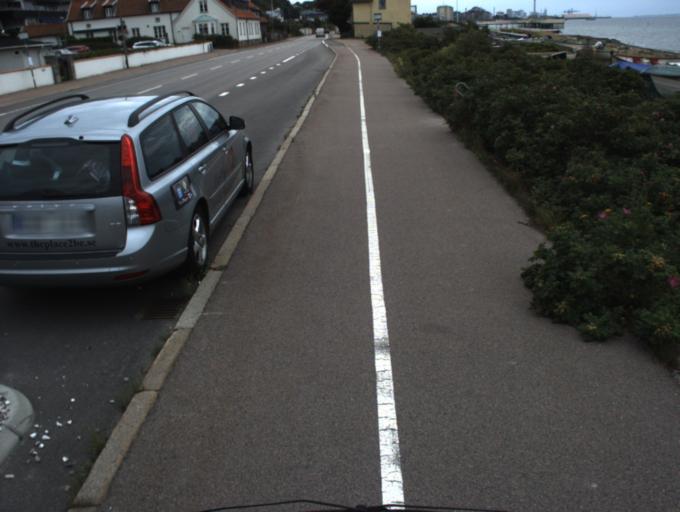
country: SE
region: Skane
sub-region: Helsingborg
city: Helsingborg
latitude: 56.0680
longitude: 12.6745
